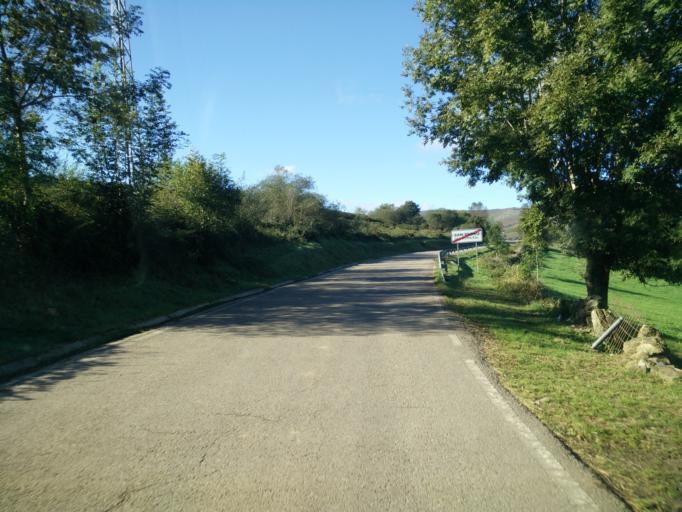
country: ES
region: Cantabria
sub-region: Provincia de Cantabria
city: San Pedro del Romeral
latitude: 43.1043
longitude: -3.8193
